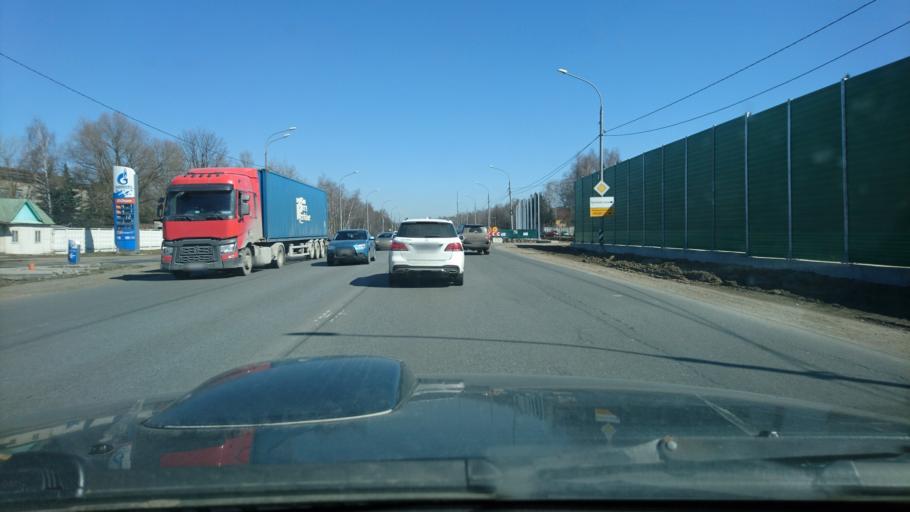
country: RU
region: Moskovskaya
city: Troitsk
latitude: 55.4742
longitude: 37.3126
